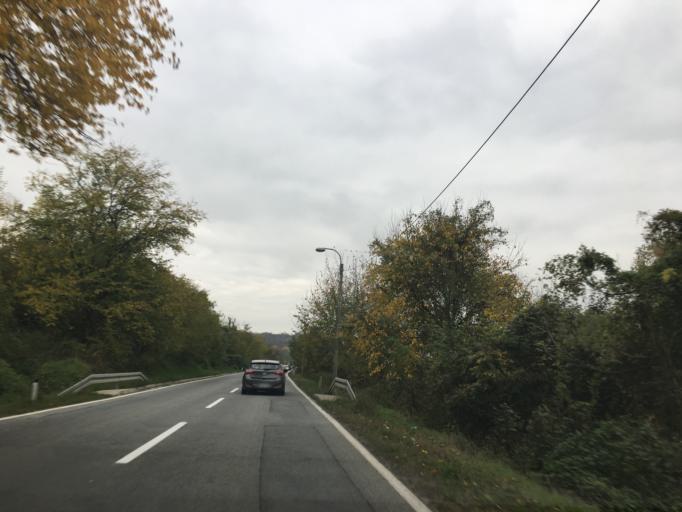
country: RS
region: Central Serbia
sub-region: Raski Okrug
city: Kraljevo
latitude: 43.7209
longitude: 20.7735
